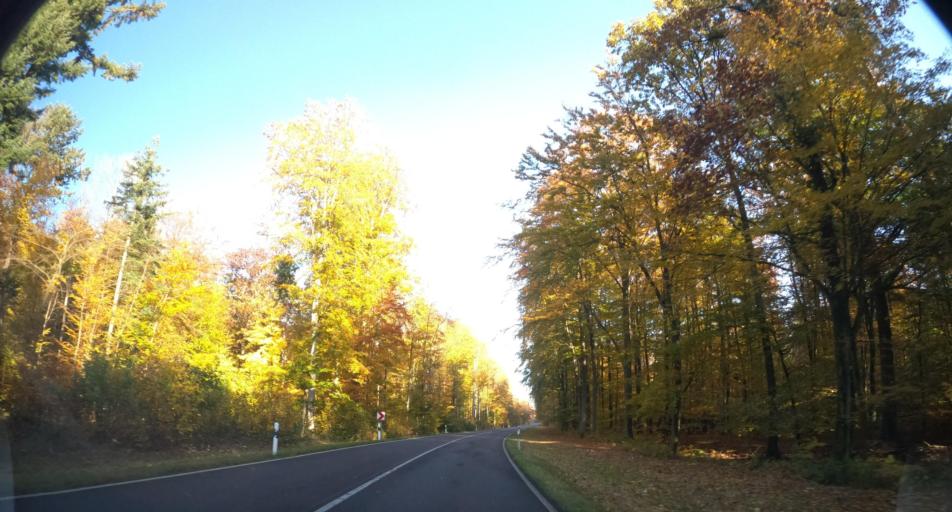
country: DE
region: Mecklenburg-Vorpommern
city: Ahlbeck
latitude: 53.6735
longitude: 14.1350
